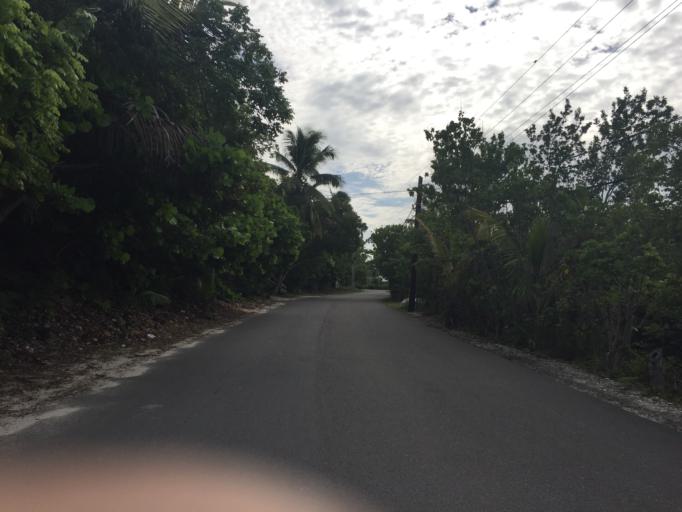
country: BS
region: Central Abaco
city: Marsh Harbour
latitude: 26.5329
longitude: -76.9603
